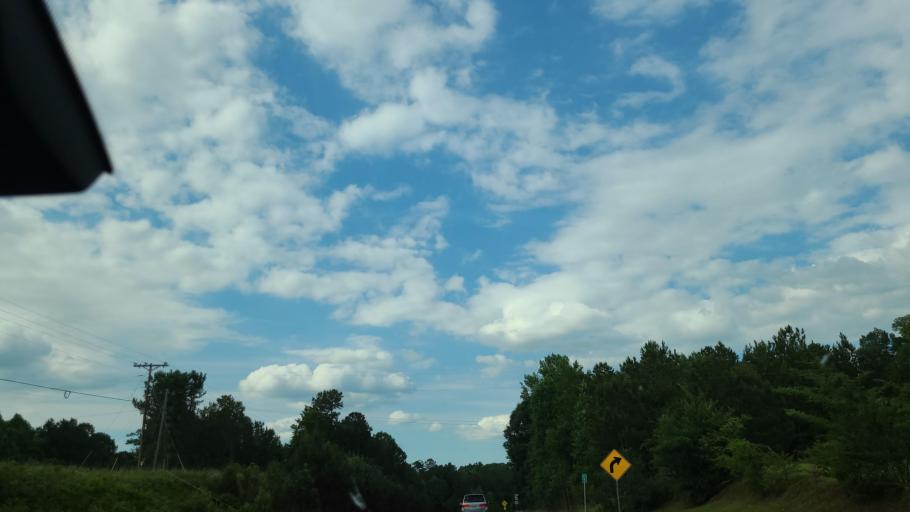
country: US
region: Georgia
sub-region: Putnam County
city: Eatonton
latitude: 33.2526
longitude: -83.4278
